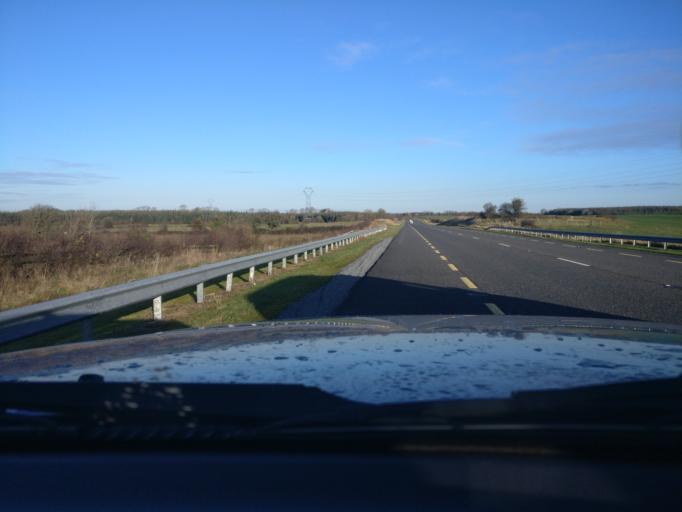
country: IE
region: Connaught
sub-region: County Galway
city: Loughrea
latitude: 53.2377
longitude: -8.5943
